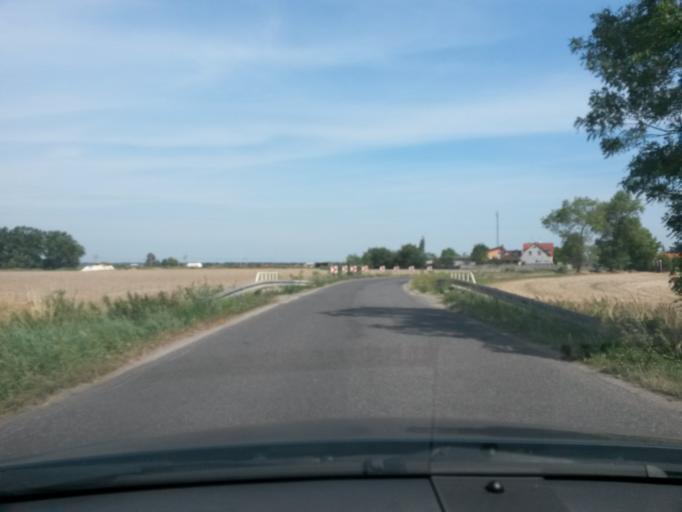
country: PL
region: Lower Silesian Voivodeship
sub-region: Powiat legnicki
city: Prochowice
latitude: 51.2115
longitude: 16.3490
